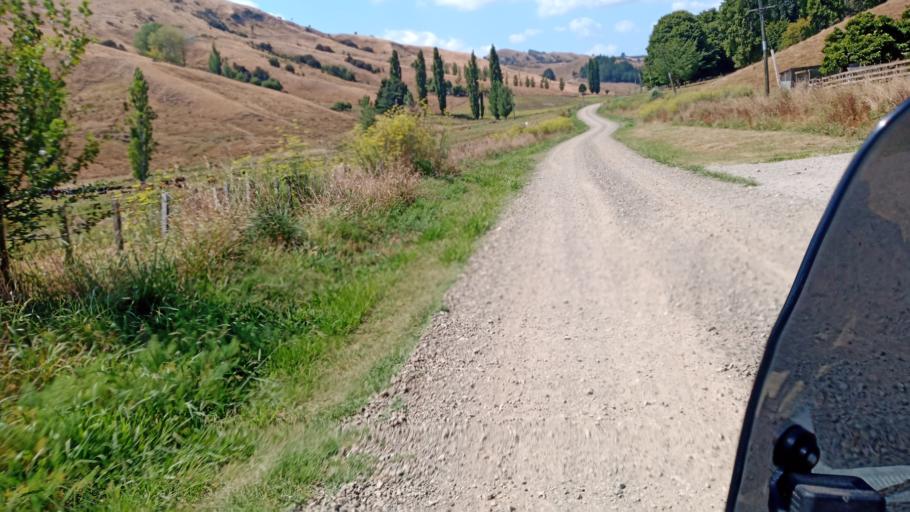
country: NZ
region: Gisborne
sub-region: Gisborne District
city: Gisborne
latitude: -38.4817
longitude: 177.8416
